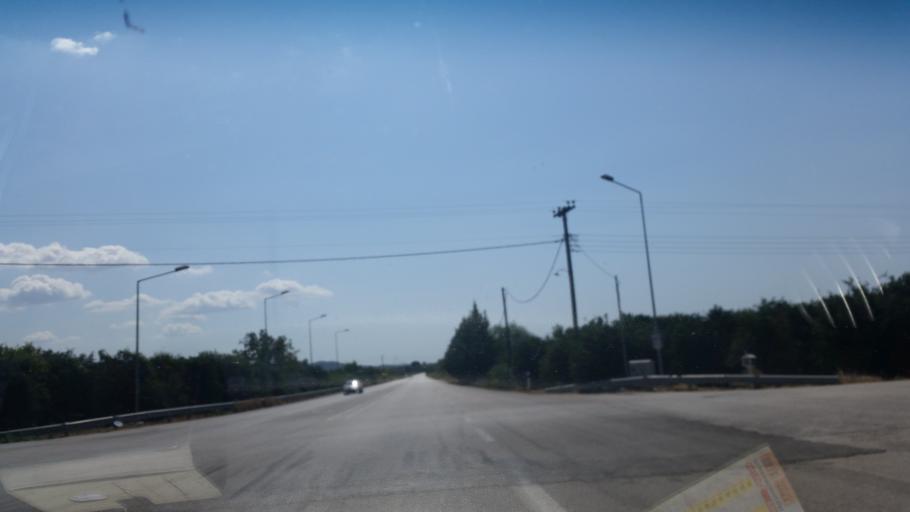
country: GR
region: Peloponnese
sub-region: Nomos Argolidos
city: Ayia Trias
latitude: 37.6583
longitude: 22.8013
